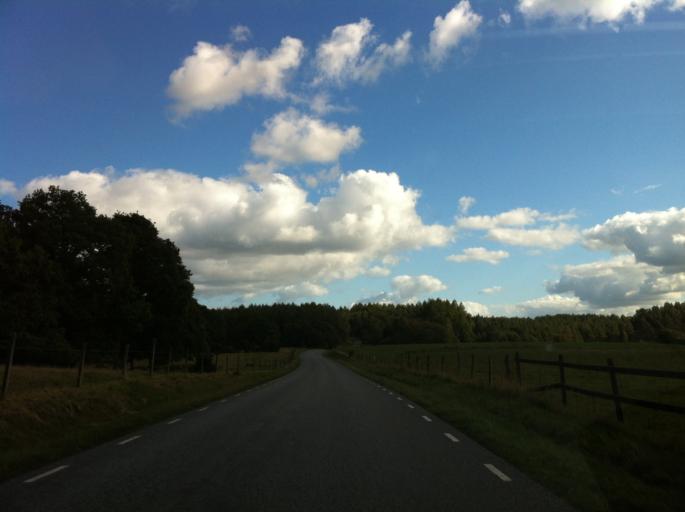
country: SE
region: Skane
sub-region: Kristianstads Kommun
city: Degeberga
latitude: 55.7098
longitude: 13.9830
